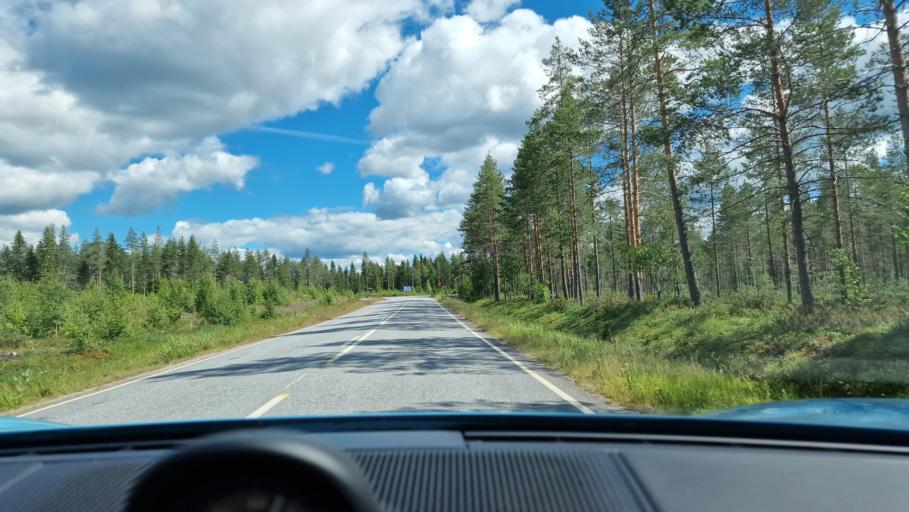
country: FI
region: Central Finland
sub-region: Saarijaervi-Viitasaari
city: Pylkoenmaeki
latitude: 62.6589
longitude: 24.5688
